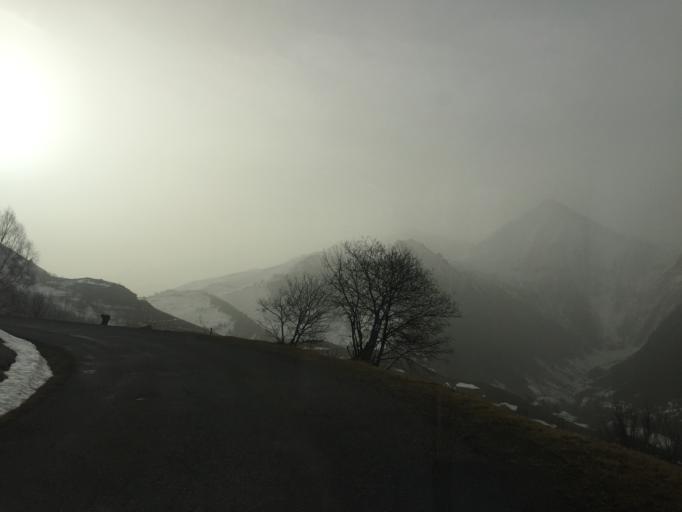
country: FR
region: Midi-Pyrenees
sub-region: Departement des Hautes-Pyrenees
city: Saint-Lary-Soulan
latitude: 42.8065
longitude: 0.3640
